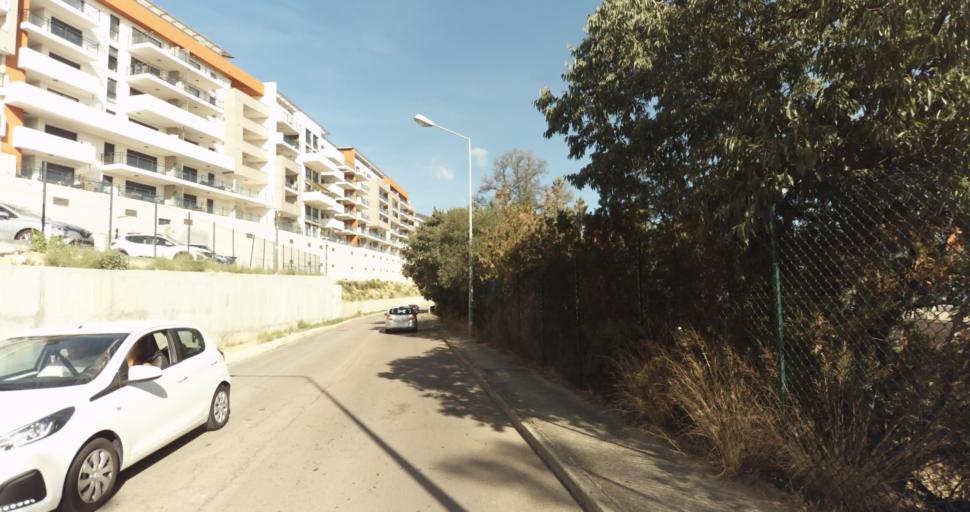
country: FR
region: Corsica
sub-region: Departement de la Corse-du-Sud
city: Ajaccio
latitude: 41.9238
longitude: 8.7303
